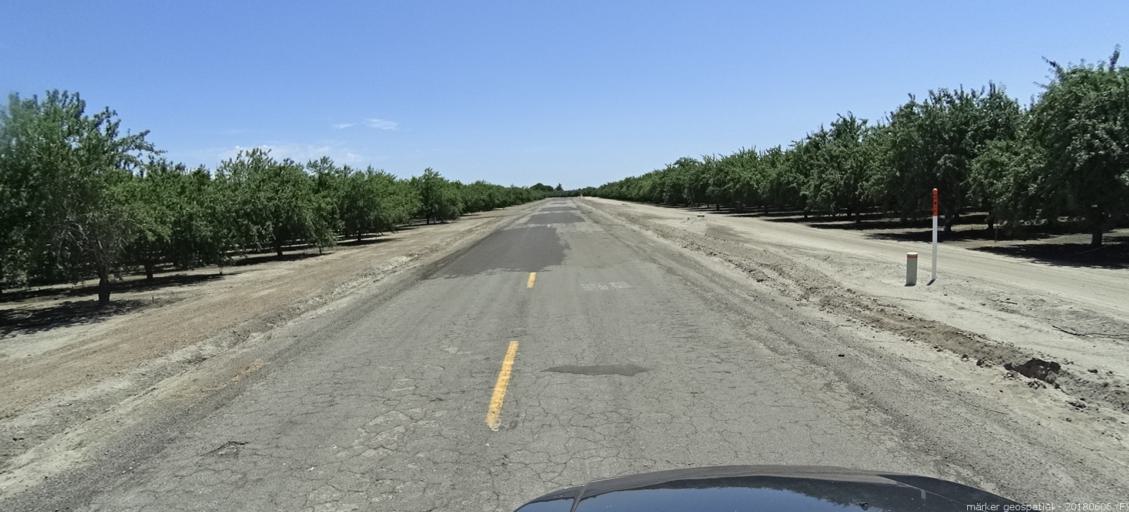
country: US
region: California
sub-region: Fresno County
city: Mendota
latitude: 36.8090
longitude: -120.3601
